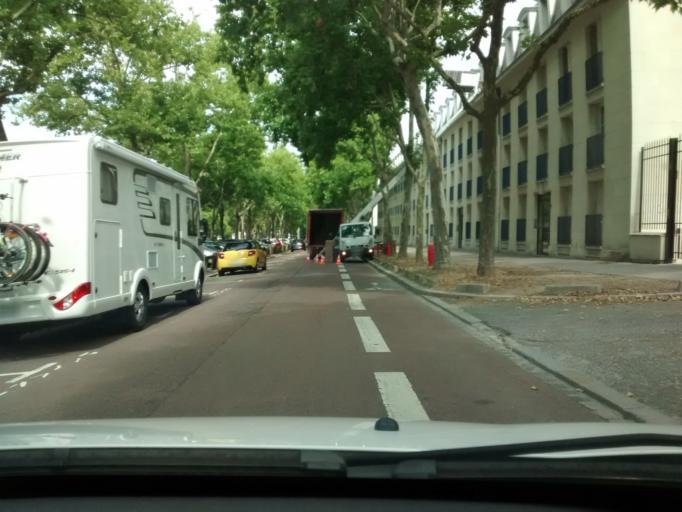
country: FR
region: Ile-de-France
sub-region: Departement des Yvelines
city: Versailles
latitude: 48.7982
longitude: 2.1301
